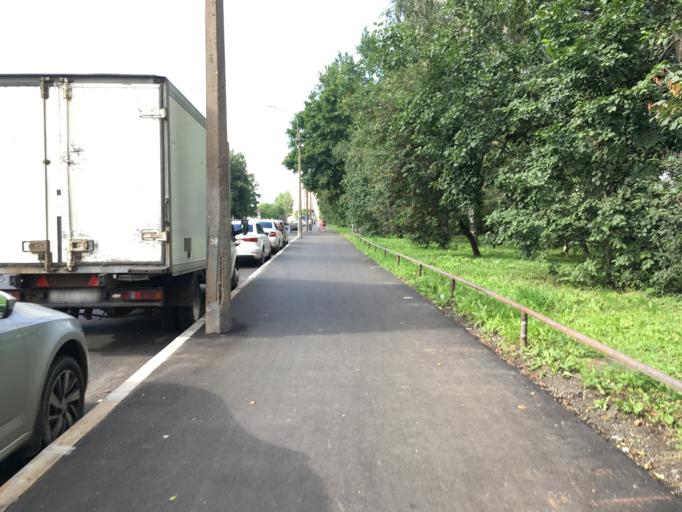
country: RU
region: St.-Petersburg
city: Obukhovo
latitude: 59.8969
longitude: 30.4621
